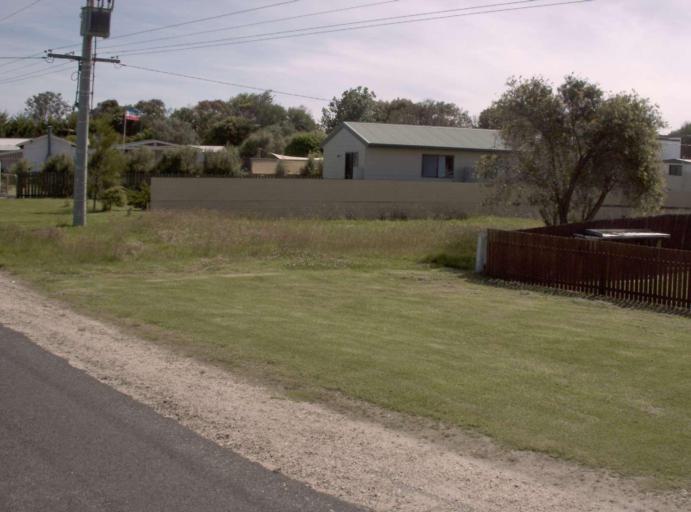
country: AU
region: Victoria
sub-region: Wellington
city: Sale
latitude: -38.3719
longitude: 147.1886
